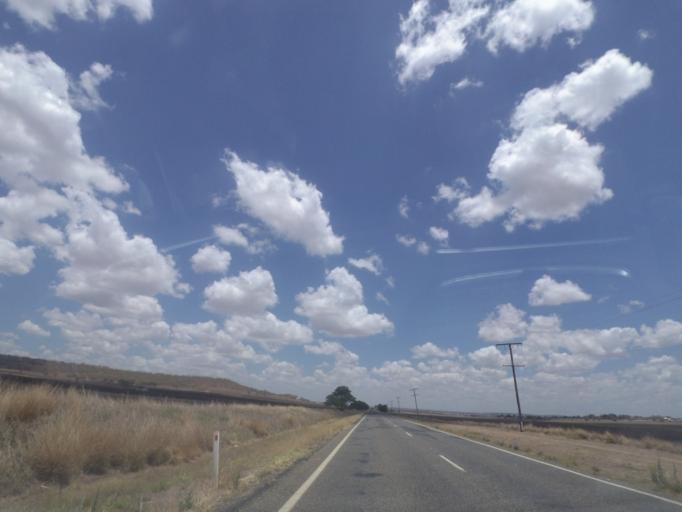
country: AU
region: Queensland
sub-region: Southern Downs
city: Warwick
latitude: -28.0058
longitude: 151.9909
